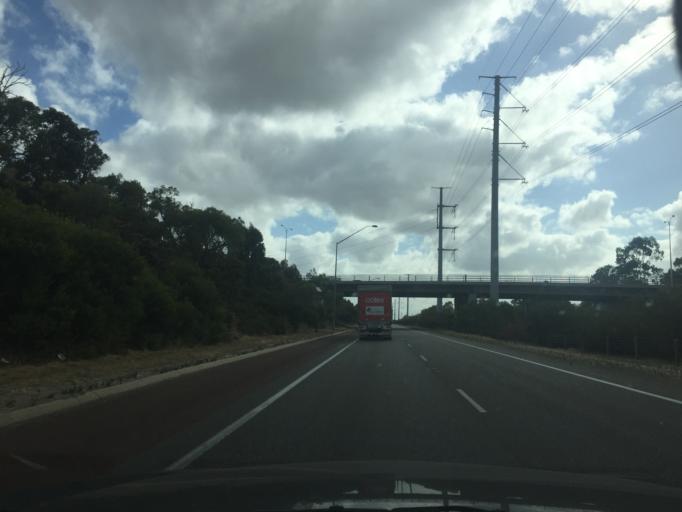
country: AU
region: Western Australia
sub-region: Gosnells
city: Langford
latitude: -32.0427
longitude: 115.9513
